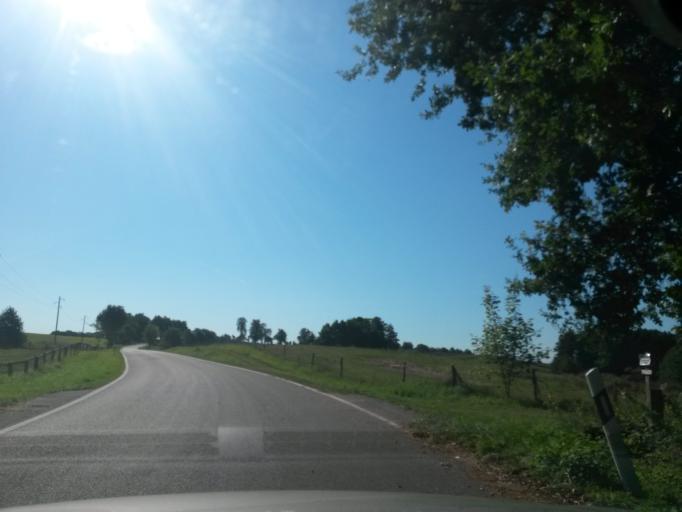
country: DE
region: Brandenburg
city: Lychen
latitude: 53.1330
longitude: 13.3821
